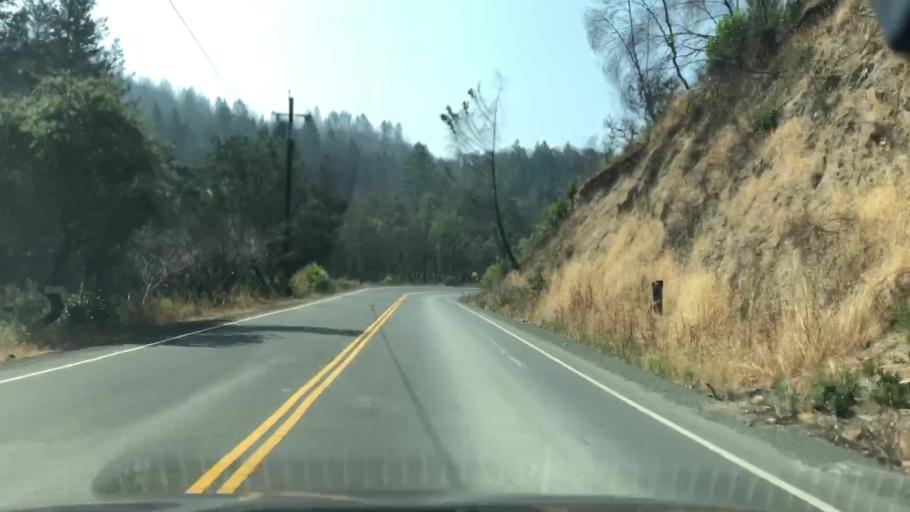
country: US
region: California
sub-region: Sonoma County
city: Larkfield-Wikiup
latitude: 38.5512
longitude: -122.6679
